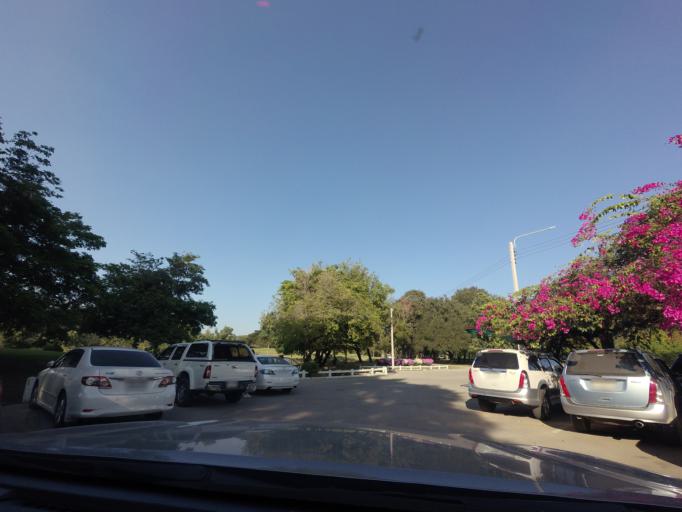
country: TH
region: Lampang
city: Mae Mo
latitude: 18.3228
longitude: 99.7451
